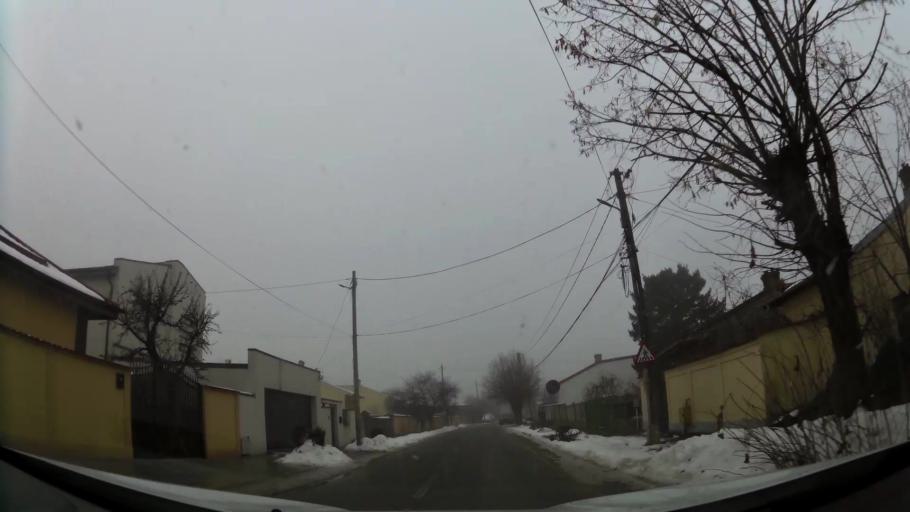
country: RO
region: Ilfov
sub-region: Comuna Chiajna
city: Chiajna
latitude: 44.4593
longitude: 25.9749
